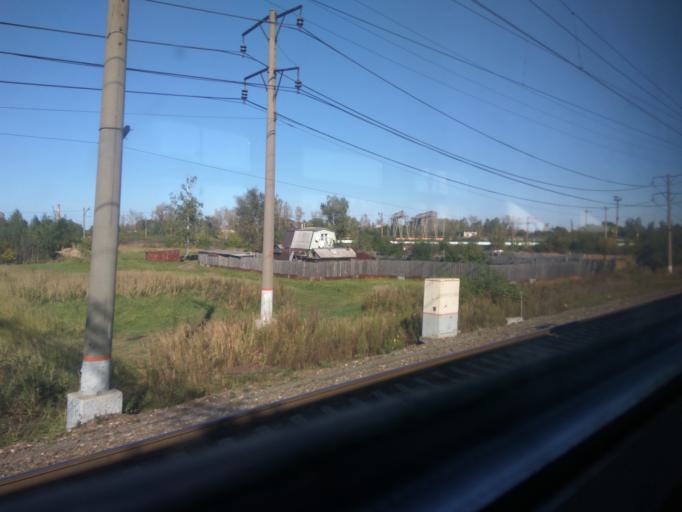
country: RU
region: Moskovskaya
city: Kurovskoye
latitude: 55.5718
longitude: 38.8984
